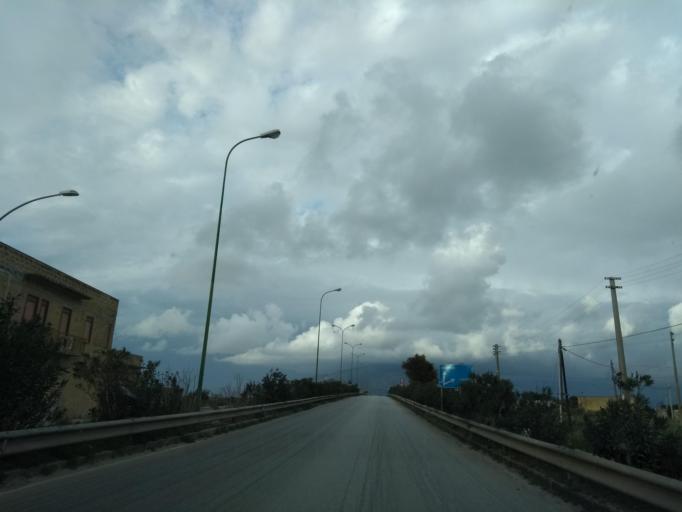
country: IT
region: Sicily
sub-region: Trapani
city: Marausa
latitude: 37.9667
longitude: 12.5200
